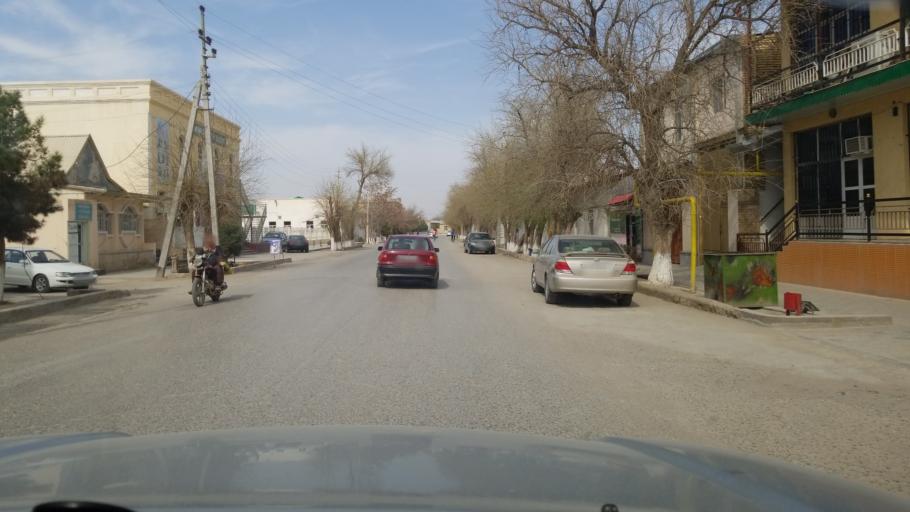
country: TM
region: Lebap
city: Atamyrat
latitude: 37.8355
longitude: 65.2119
